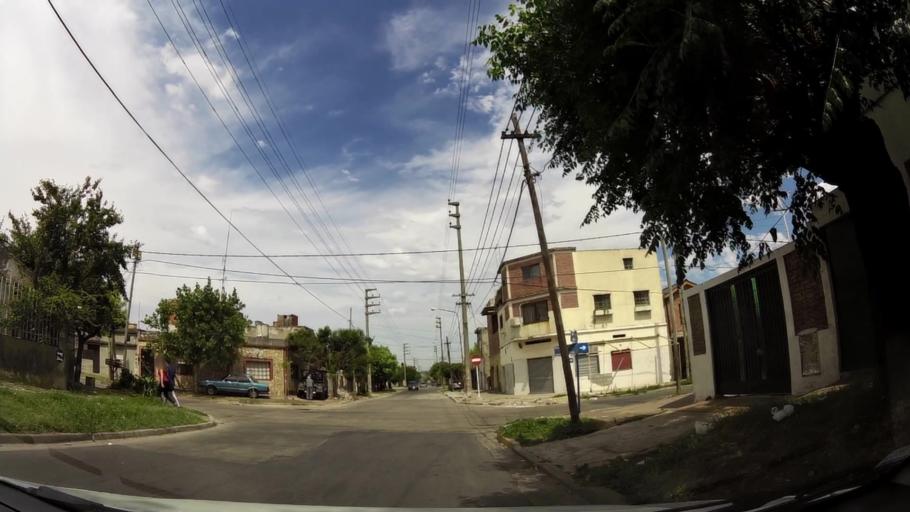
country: AR
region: Buenos Aires
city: San Justo
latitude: -34.6914
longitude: -58.5466
